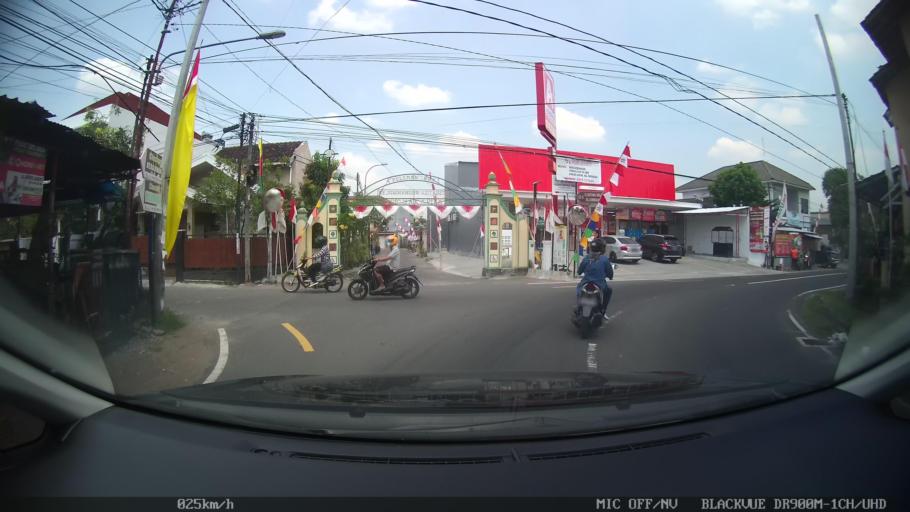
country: ID
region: Daerah Istimewa Yogyakarta
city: Yogyakarta
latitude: -7.8132
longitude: 110.3962
